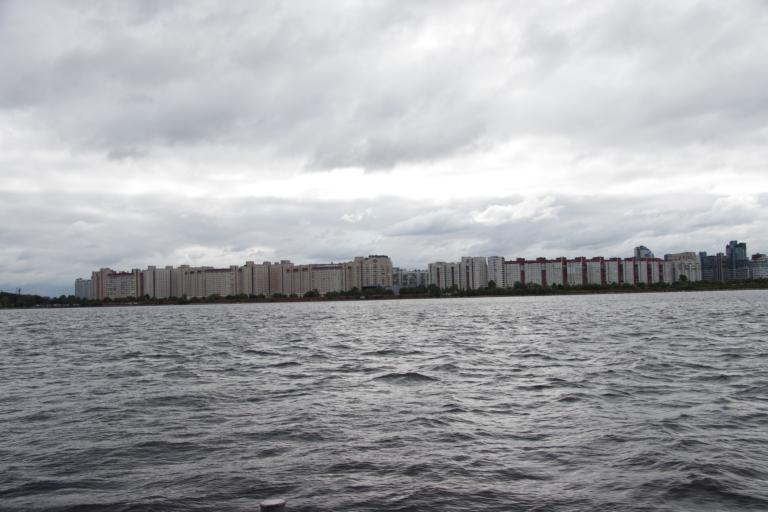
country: RU
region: St.-Petersburg
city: Staraya Derevnya
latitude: 59.9670
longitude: 30.2104
